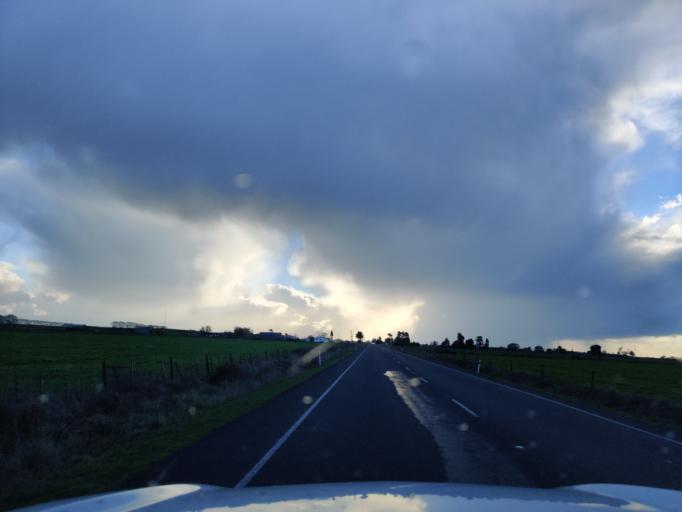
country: NZ
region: Waikato
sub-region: Hamilton City
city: Hamilton
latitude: -37.6932
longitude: 175.4319
